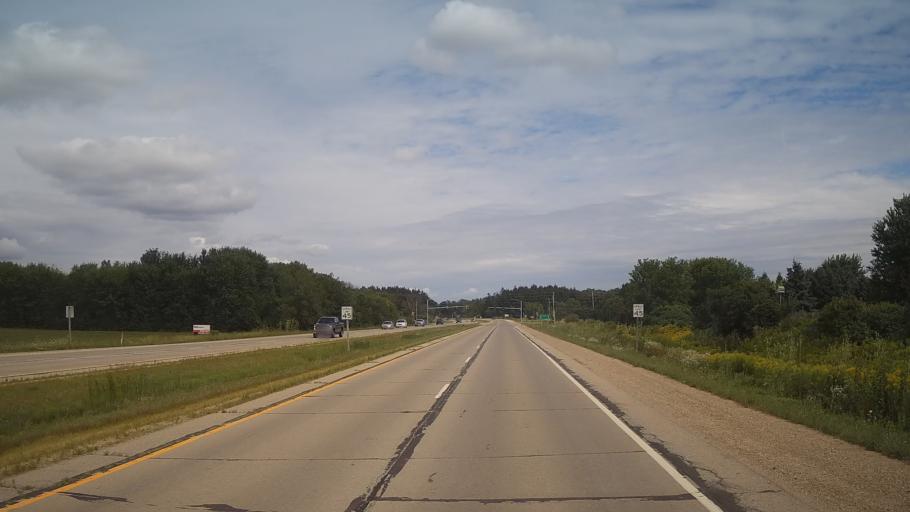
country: US
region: Wisconsin
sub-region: Winnebago County
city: Oshkosh
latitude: 44.0286
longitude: -88.6070
